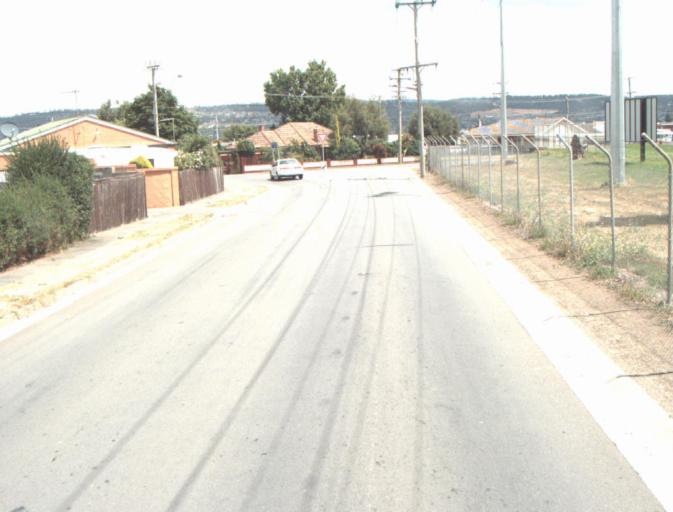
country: AU
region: Tasmania
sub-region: Launceston
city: Newnham
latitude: -41.4067
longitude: 147.1436
